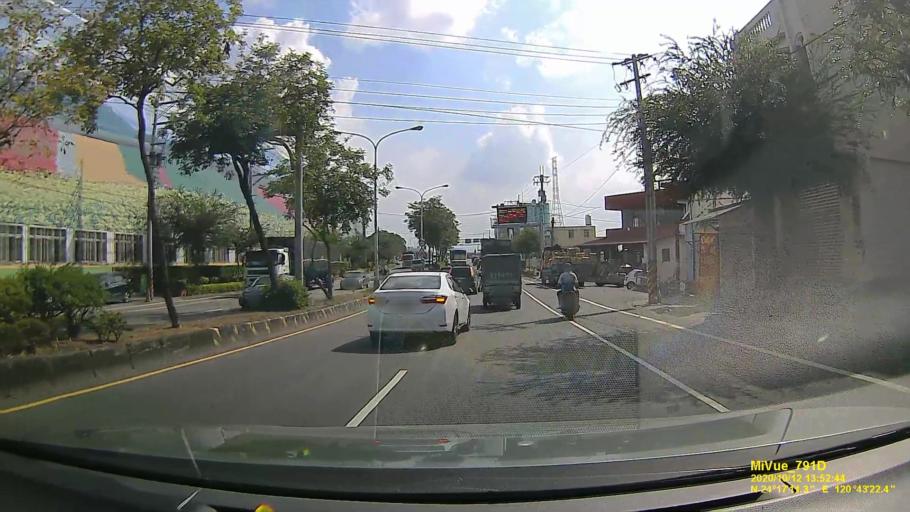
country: TW
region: Taiwan
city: Fengyuan
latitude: 24.2864
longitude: 120.7229
